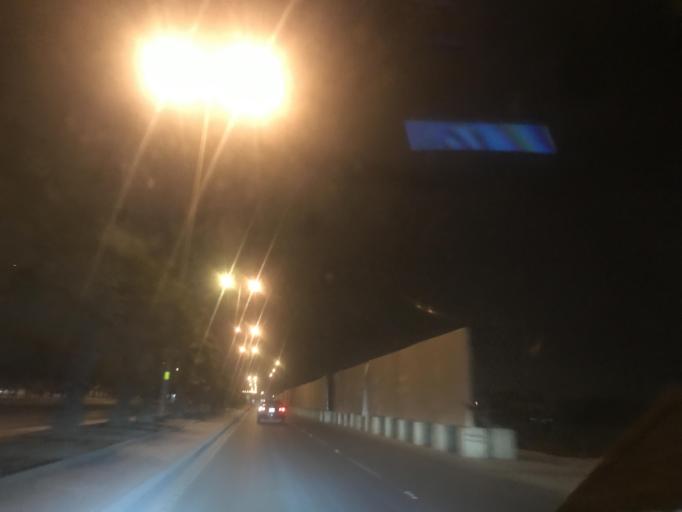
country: SA
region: Ar Riyad
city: Riyadh
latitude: 24.7923
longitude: 46.5877
